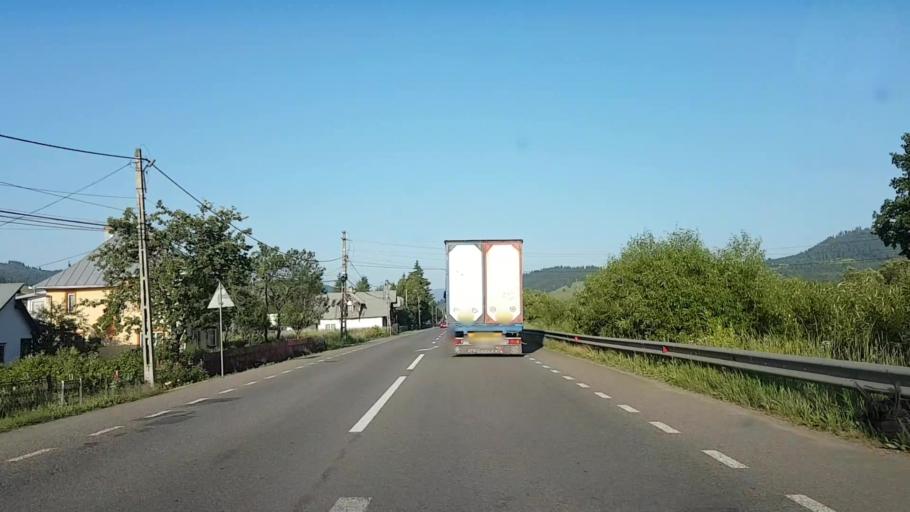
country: RO
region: Suceava
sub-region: Comuna Dorna Candrenilor
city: Dorna Candrenilor
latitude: 47.3566
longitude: 25.2376
